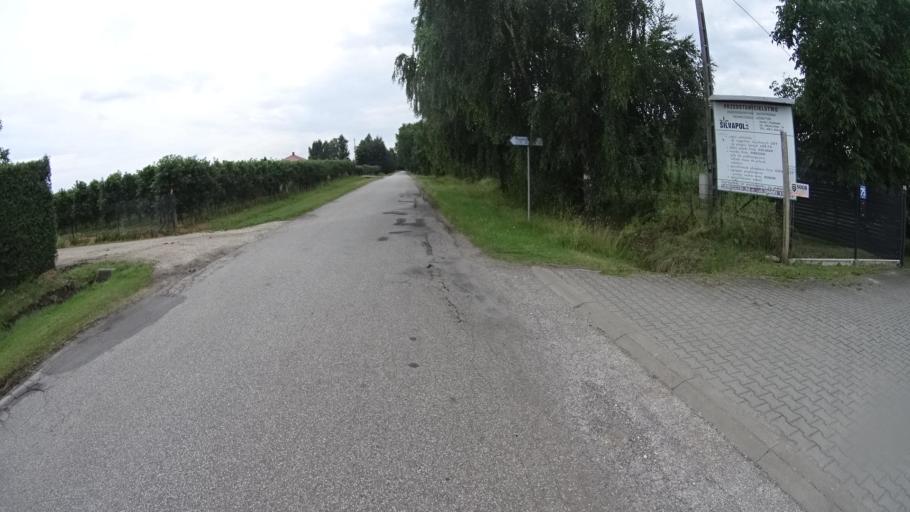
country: PL
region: Masovian Voivodeship
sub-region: Powiat grojecki
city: Goszczyn
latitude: 51.7876
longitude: 20.8557
